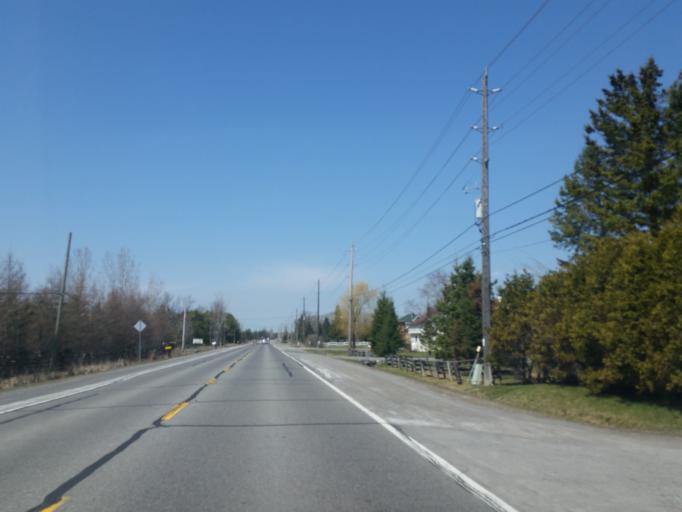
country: CA
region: Ontario
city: Bells Corners
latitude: 45.4439
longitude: -76.0506
